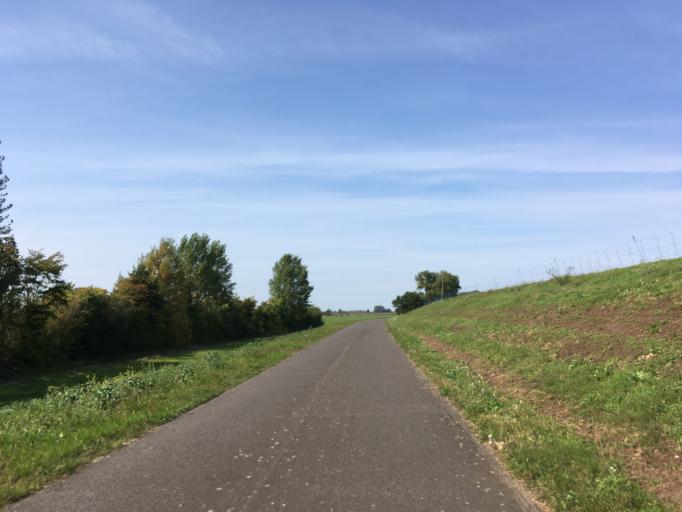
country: DE
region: Brandenburg
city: Vogelsang
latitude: 52.1869
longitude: 14.6847
